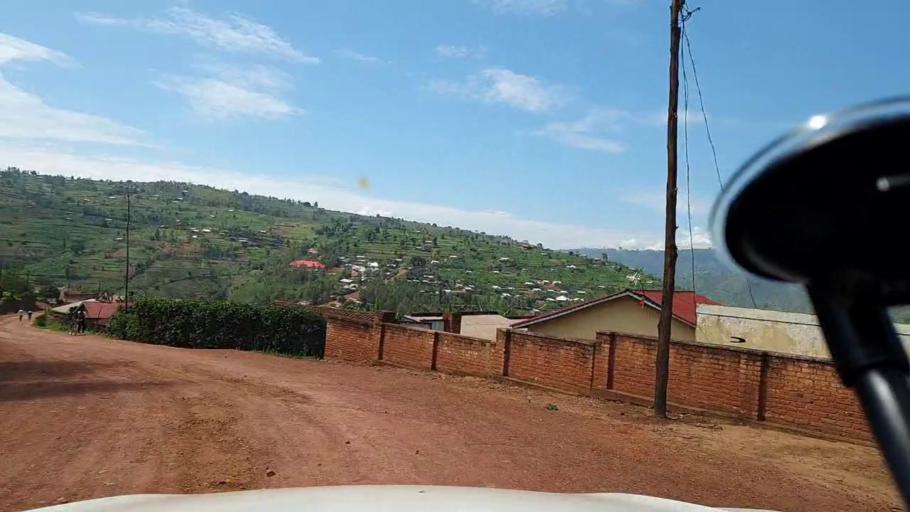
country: RW
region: Kigali
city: Kigali
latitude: -1.8001
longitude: 29.8949
